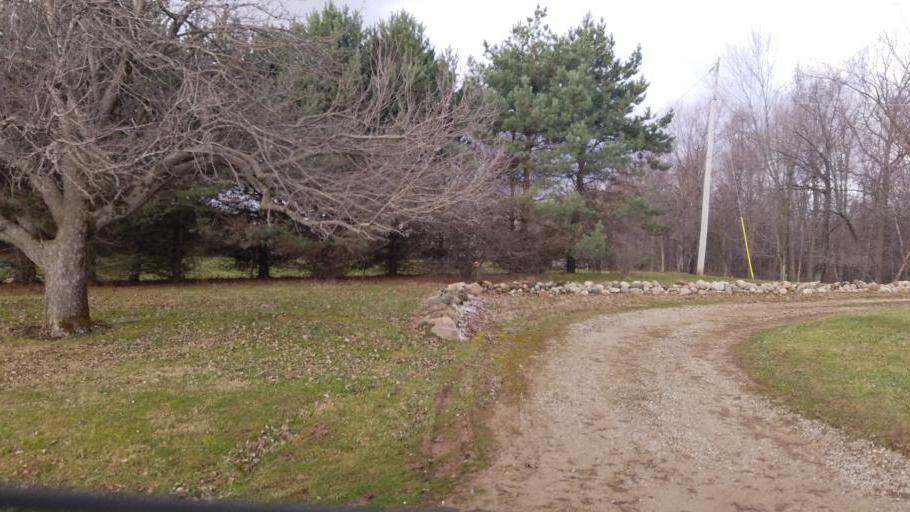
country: US
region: Ohio
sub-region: Morrow County
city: Mount Gilead
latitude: 40.5385
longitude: -82.7013
